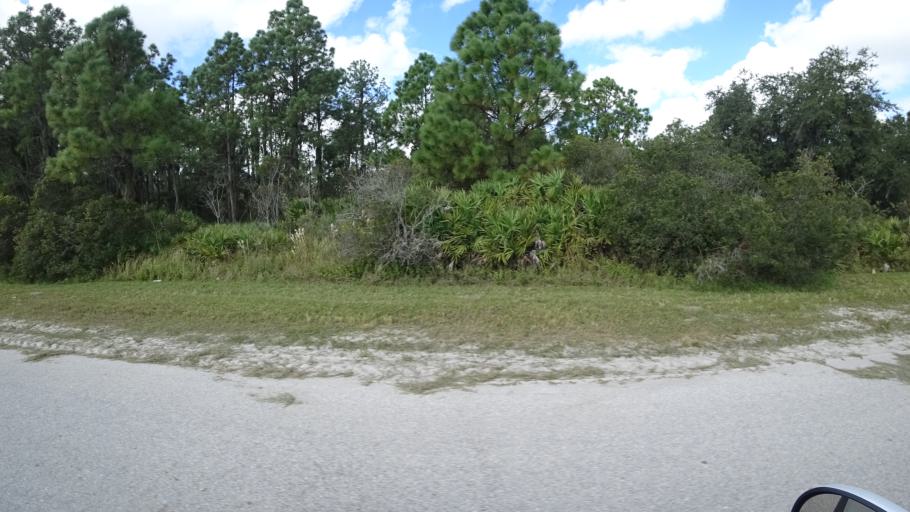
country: US
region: Florida
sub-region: Hillsborough County
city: Wimauma
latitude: 27.4565
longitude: -82.1838
